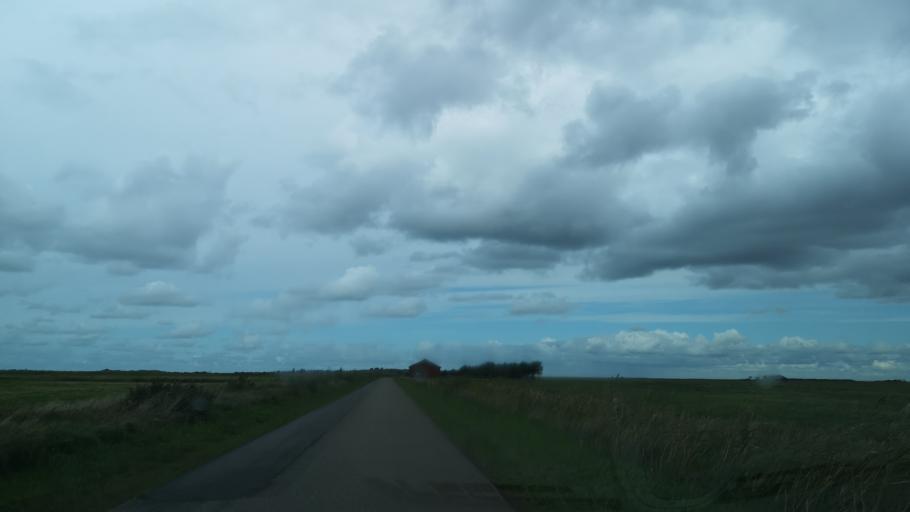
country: DK
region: Central Jutland
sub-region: Ringkobing-Skjern Kommune
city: Hvide Sande
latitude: 55.8390
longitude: 8.2175
